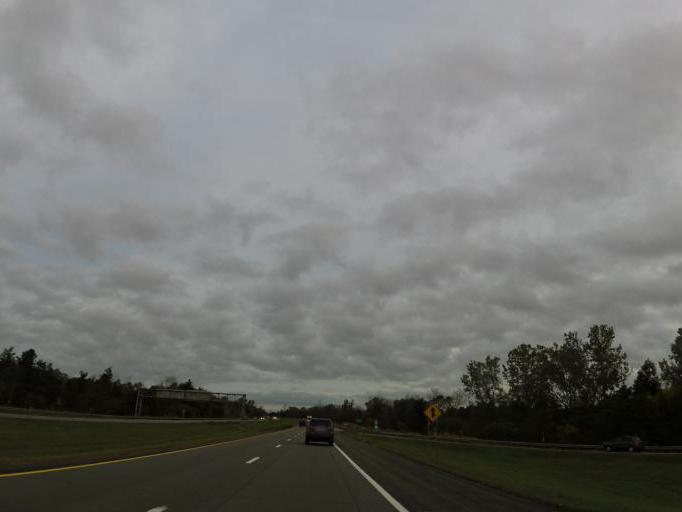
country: US
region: New York
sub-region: Erie County
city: Elma Center
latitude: 42.8359
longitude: -78.7001
